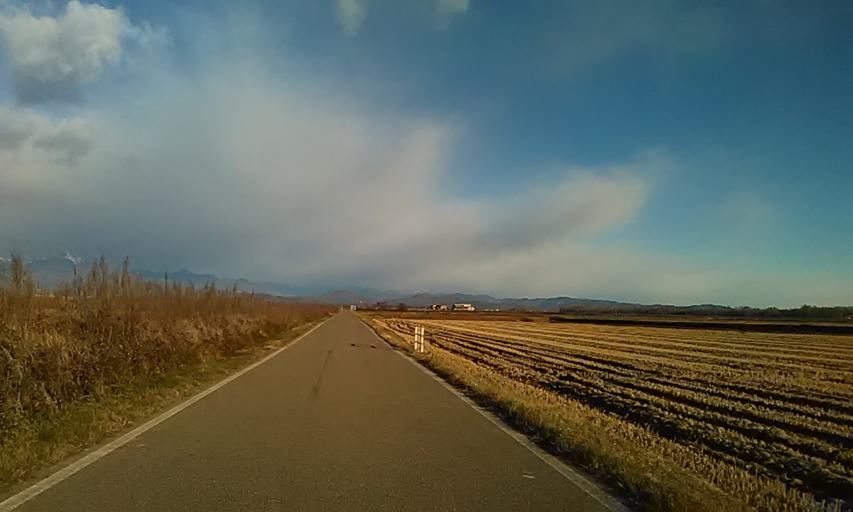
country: IT
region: Piedmont
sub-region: Provincia di Vercelli
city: Buronzo
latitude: 45.5131
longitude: 8.2701
